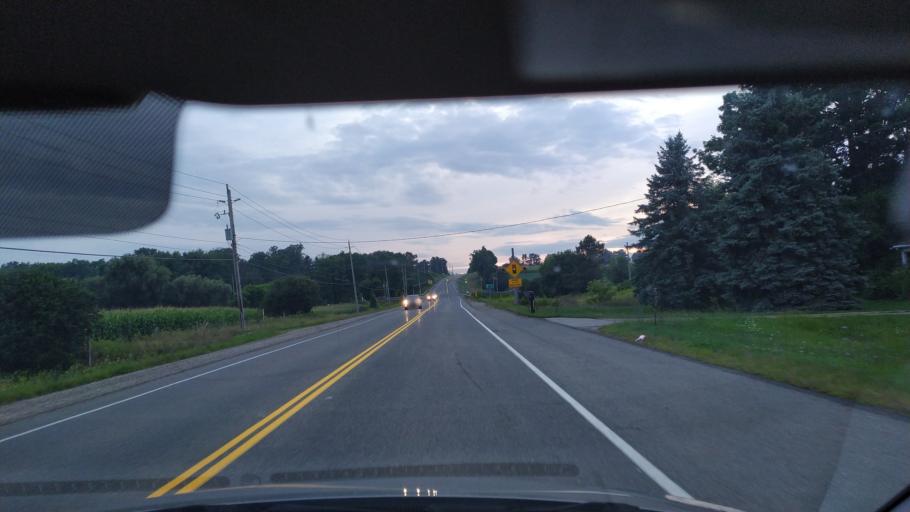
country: CA
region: Ontario
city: Kitchener
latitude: 43.3264
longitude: -80.4766
